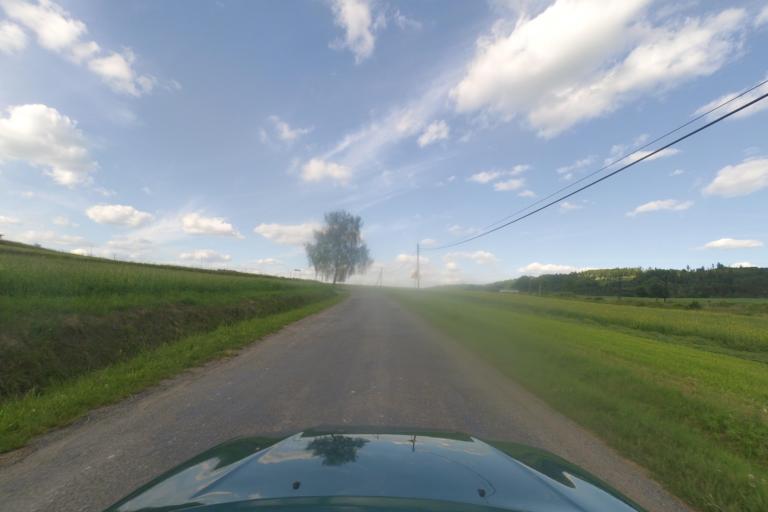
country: PL
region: Lower Silesian Voivodeship
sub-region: Powiat klodzki
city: Klodzko
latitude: 50.4787
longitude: 16.6707
